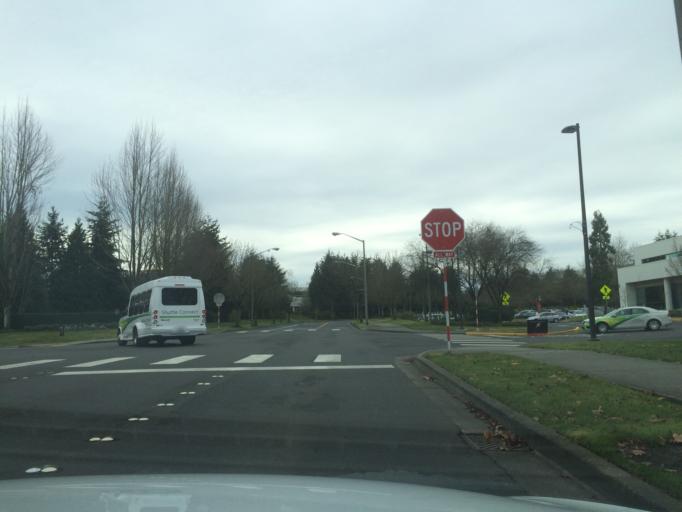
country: US
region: Washington
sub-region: King County
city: Redmond
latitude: 47.6400
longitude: -122.1306
